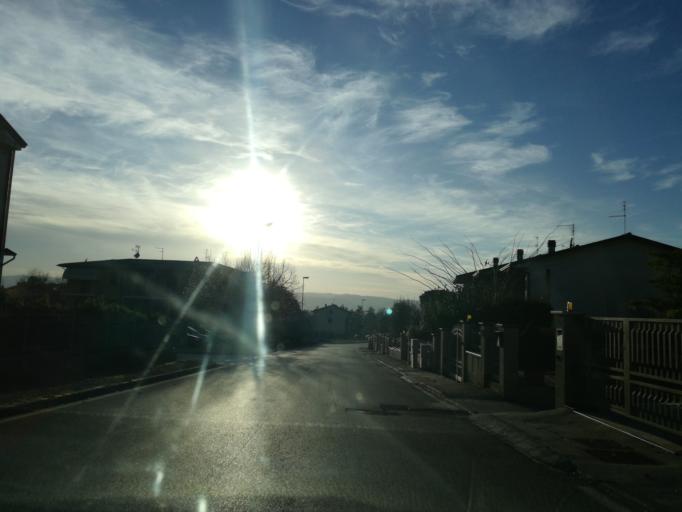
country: IT
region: Umbria
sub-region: Provincia di Perugia
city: Rivotorto
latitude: 43.0462
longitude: 12.6203
